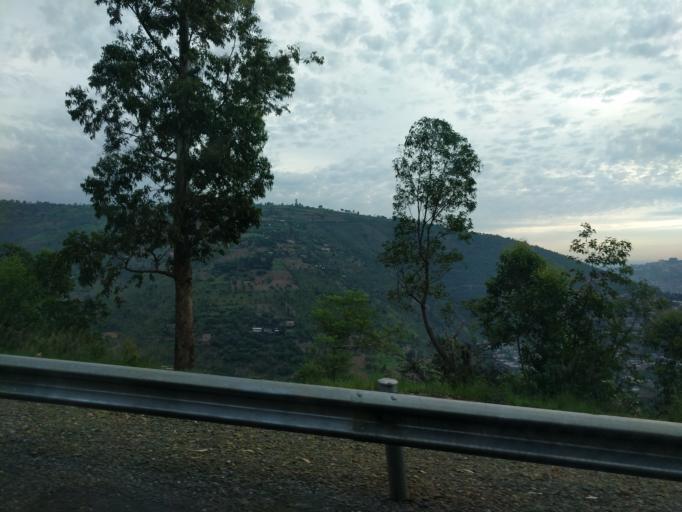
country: RW
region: Kigali
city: Kigali
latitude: -1.9382
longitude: 30.0281
